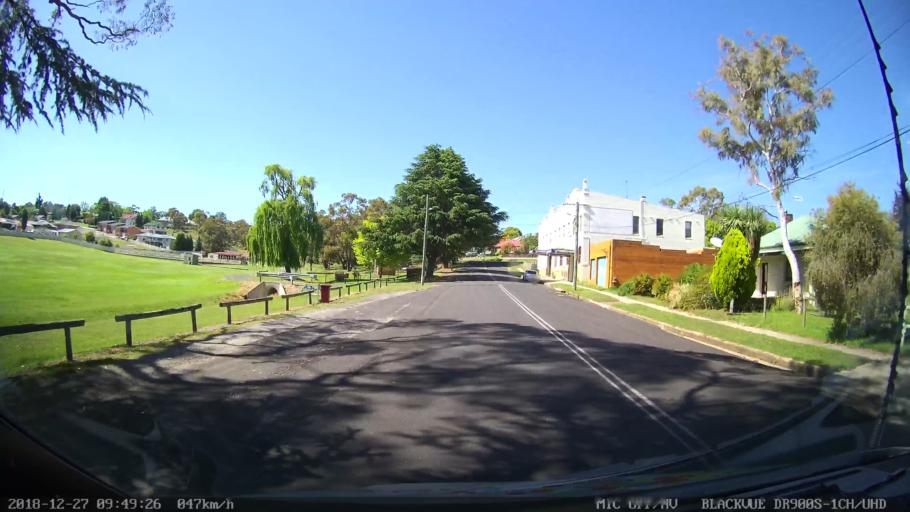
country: AU
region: New South Wales
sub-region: Lithgow
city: Portland
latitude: -33.3542
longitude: 149.9821
